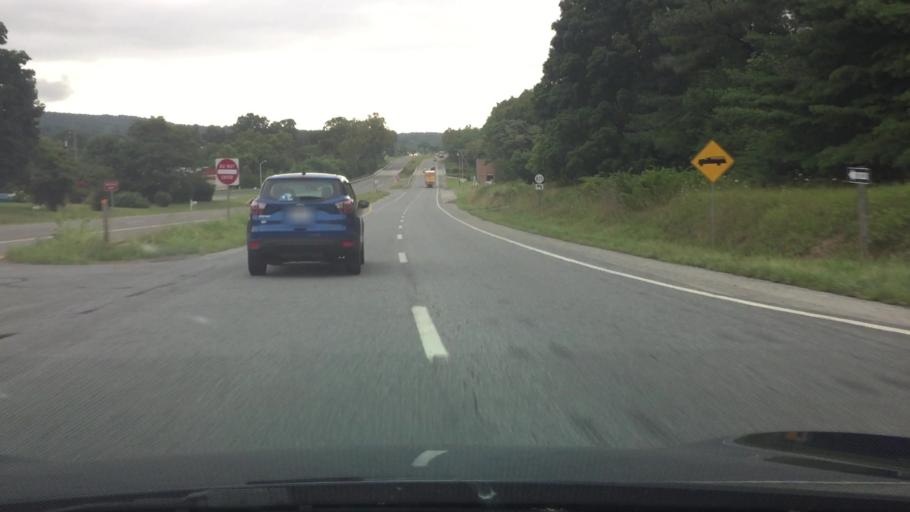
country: US
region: Virginia
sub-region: Montgomery County
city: Shawsville
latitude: 37.2260
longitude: -80.2125
